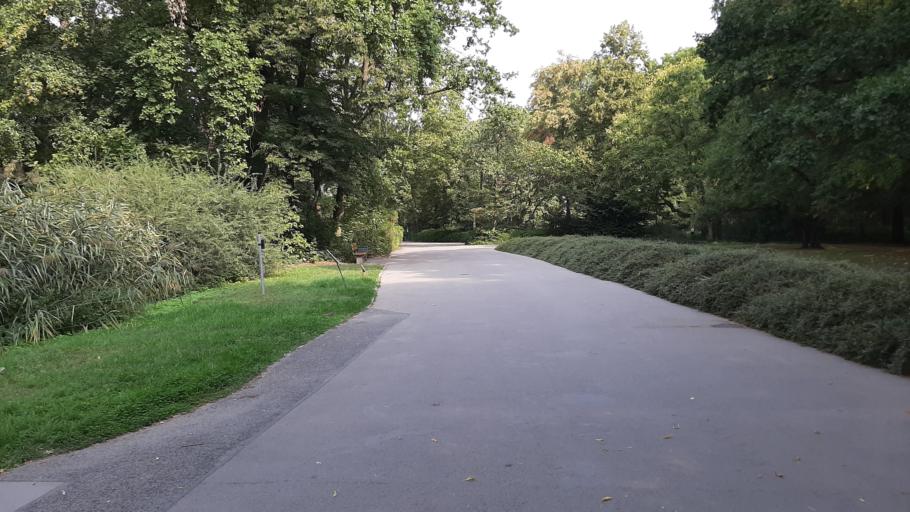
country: DE
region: Berlin
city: Karlshorst
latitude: 52.5031
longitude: 13.5300
